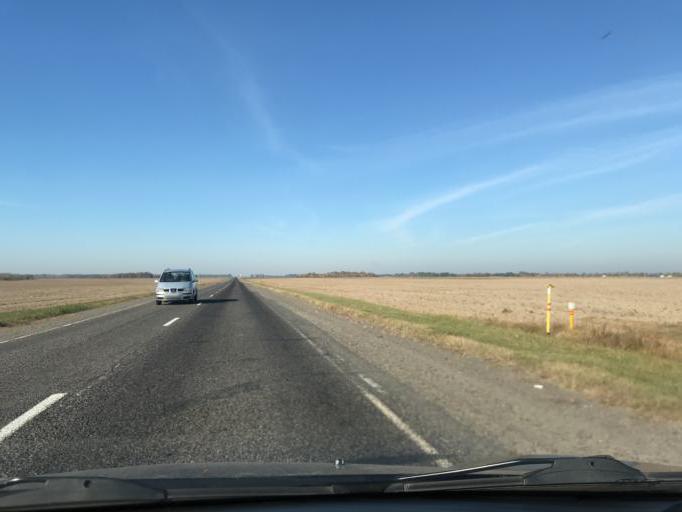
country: BY
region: Gomel
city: Brahin
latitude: 51.7862
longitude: 30.2008
